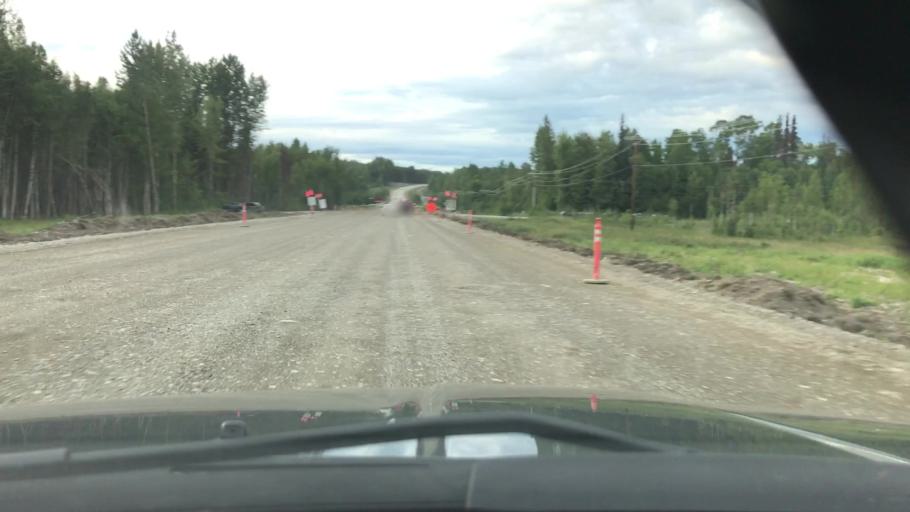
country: US
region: Alaska
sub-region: Matanuska-Susitna Borough
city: Y
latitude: 62.0990
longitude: -150.0611
